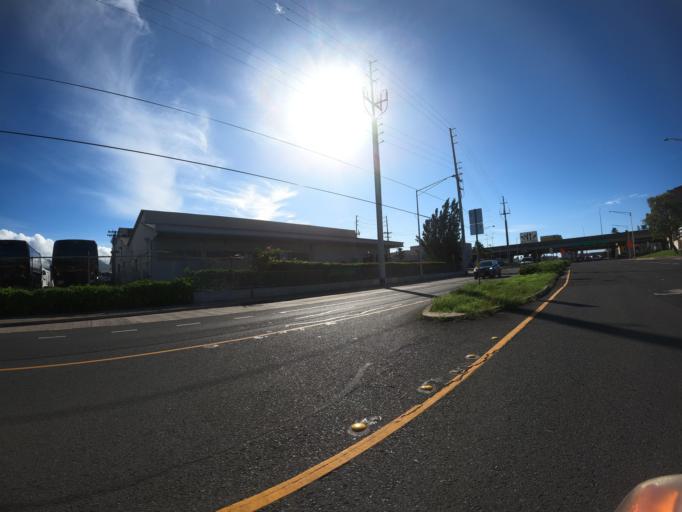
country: US
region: Hawaii
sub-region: Honolulu County
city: Halawa Heights
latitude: 21.3367
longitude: -157.9014
